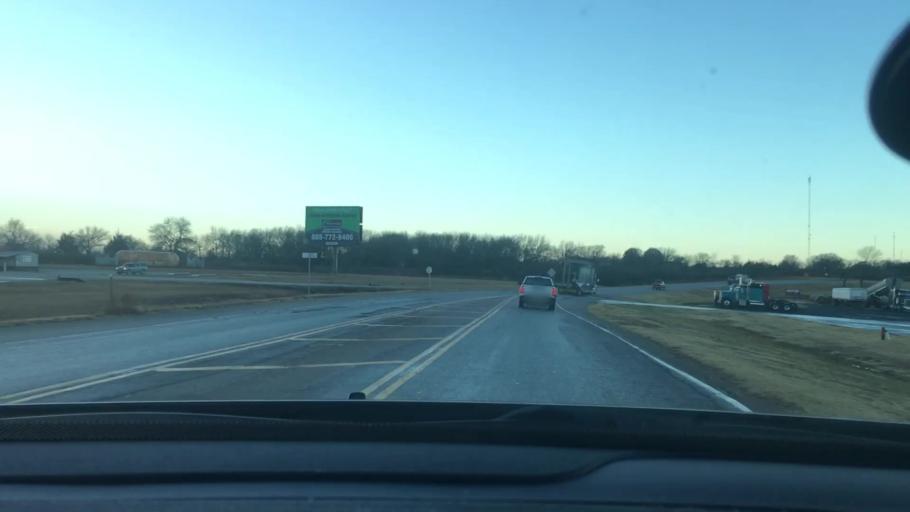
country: US
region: Oklahoma
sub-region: Pontotoc County
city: Ada
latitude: 34.7523
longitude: -96.7016
